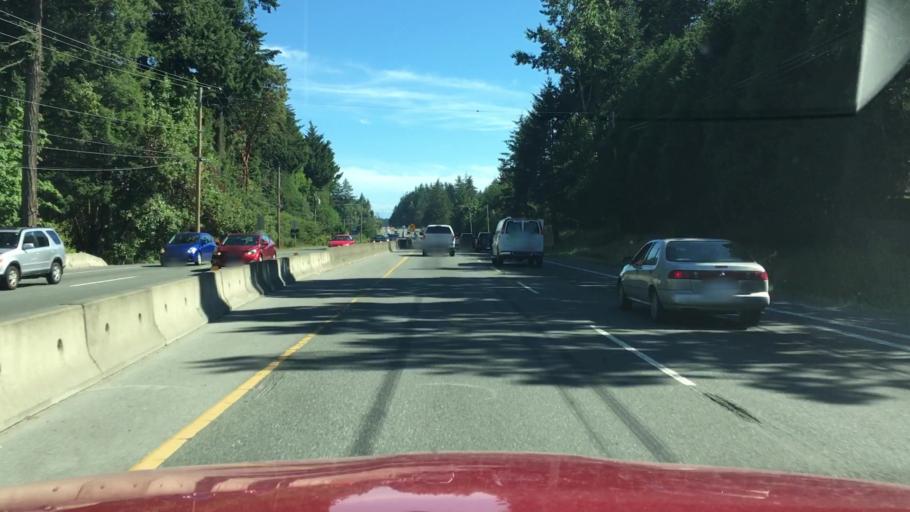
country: CA
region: British Columbia
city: North Saanich
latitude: 48.5513
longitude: -123.3924
